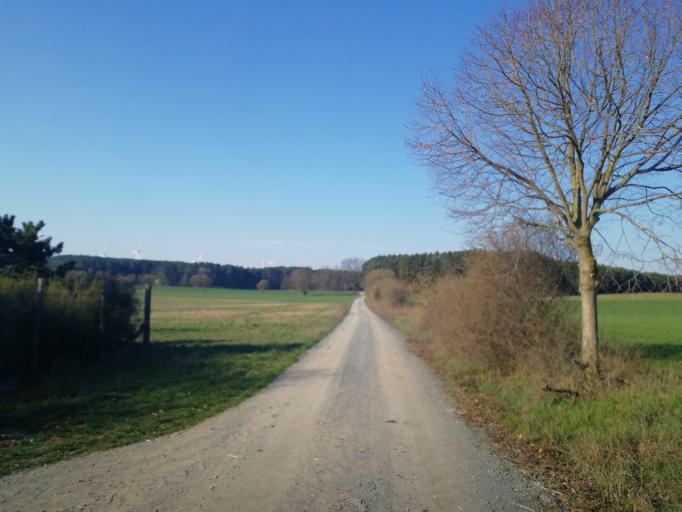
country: DE
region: Brandenburg
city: Drahnsdorf
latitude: 51.9003
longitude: 13.5389
